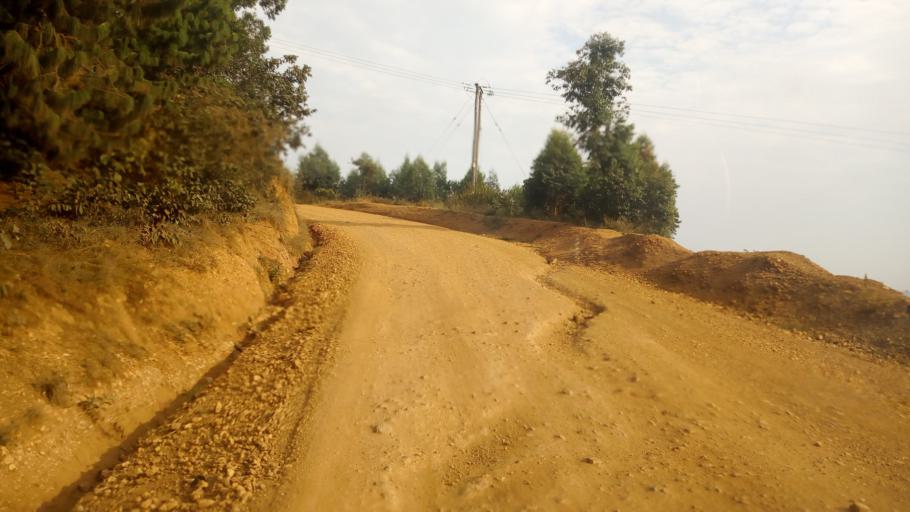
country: UG
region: Western Region
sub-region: Kanungu District
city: Ntungamo
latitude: -0.8313
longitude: 29.6948
